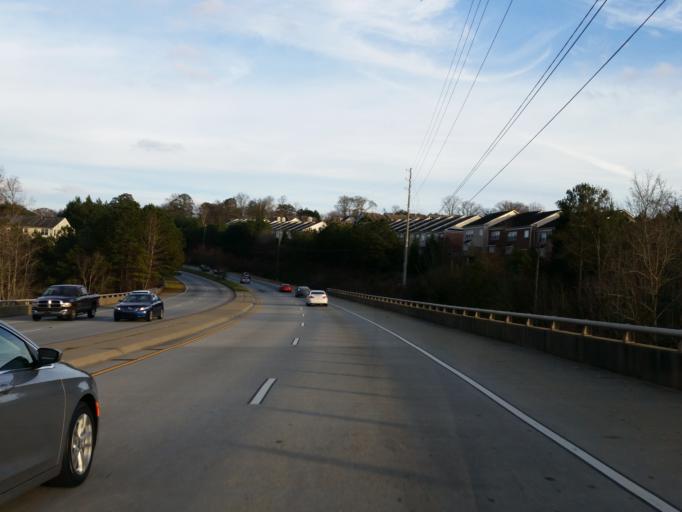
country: US
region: Georgia
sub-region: Cobb County
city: Smyrna
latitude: 33.8384
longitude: -84.5147
